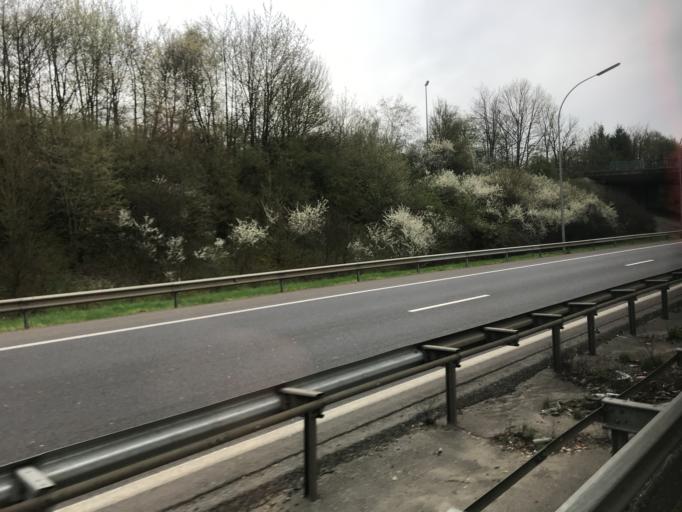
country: LU
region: Luxembourg
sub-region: Canton d'Esch-sur-Alzette
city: Leudelange
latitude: 49.5680
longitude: 6.0862
